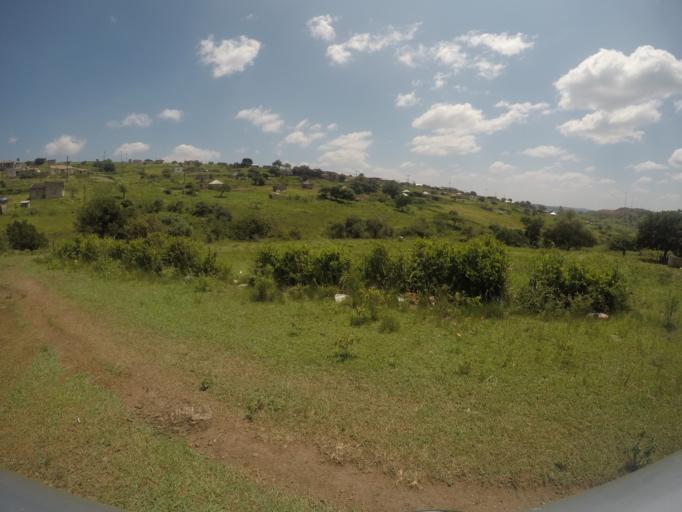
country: ZA
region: KwaZulu-Natal
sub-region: uThungulu District Municipality
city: Empangeni
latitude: -28.6076
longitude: 31.7359
